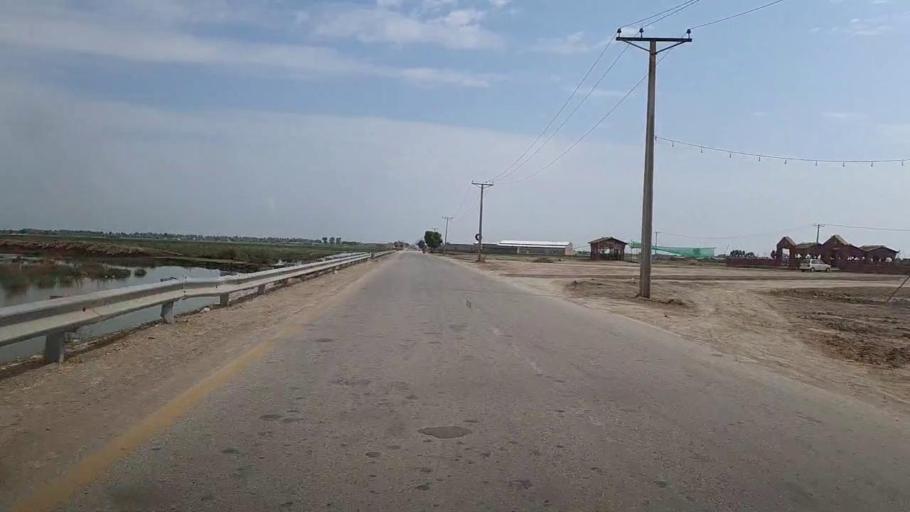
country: PK
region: Sindh
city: Thul
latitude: 28.2569
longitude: 68.7784
